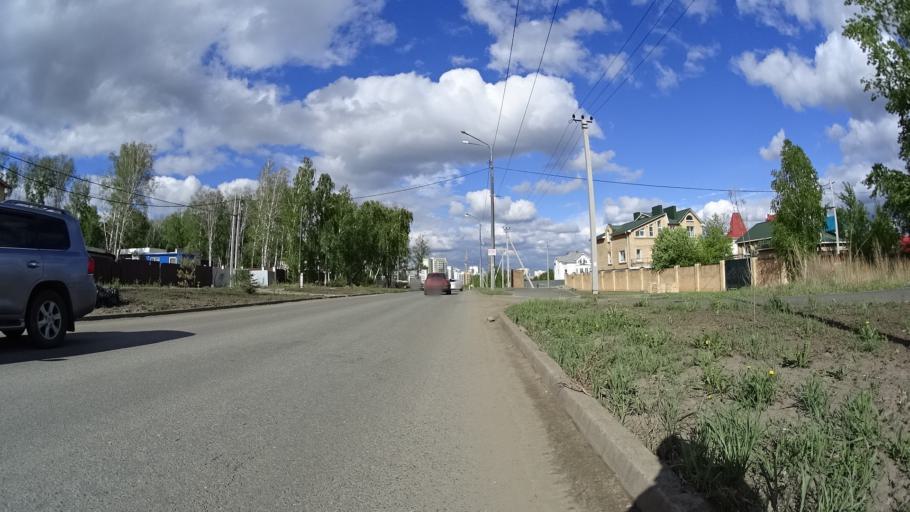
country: RU
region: Chelyabinsk
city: Sargazy
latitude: 55.1557
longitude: 61.2813
